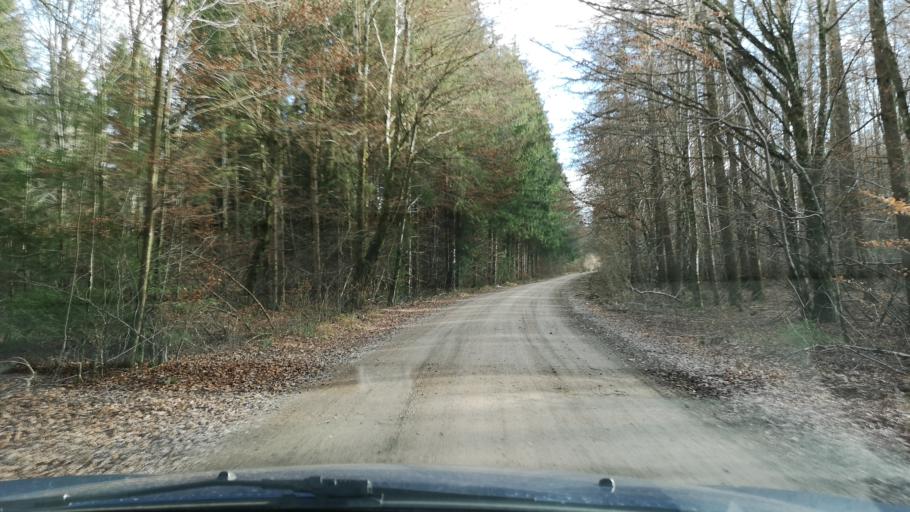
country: DE
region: Bavaria
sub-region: Upper Bavaria
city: Ebersberg
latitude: 48.1086
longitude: 11.9278
